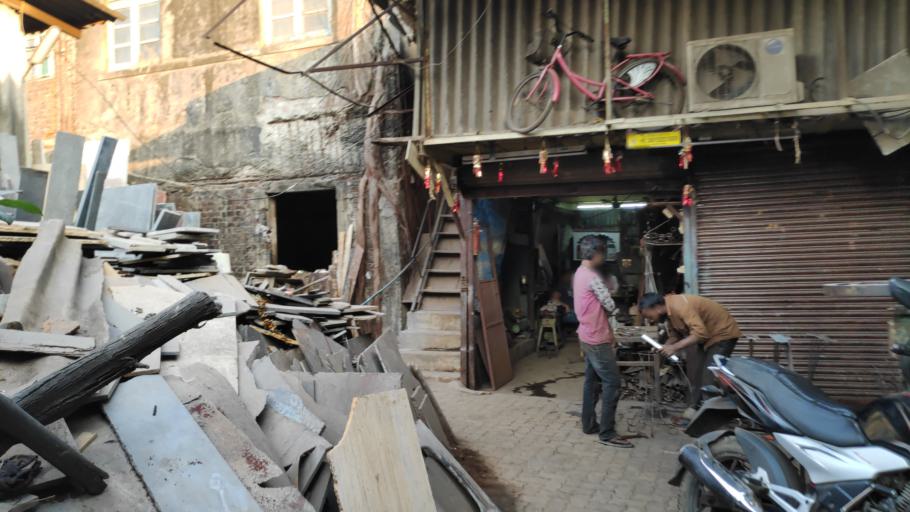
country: IN
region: Maharashtra
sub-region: Mumbai Suburban
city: Mumbai
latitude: 19.0753
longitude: 72.8483
